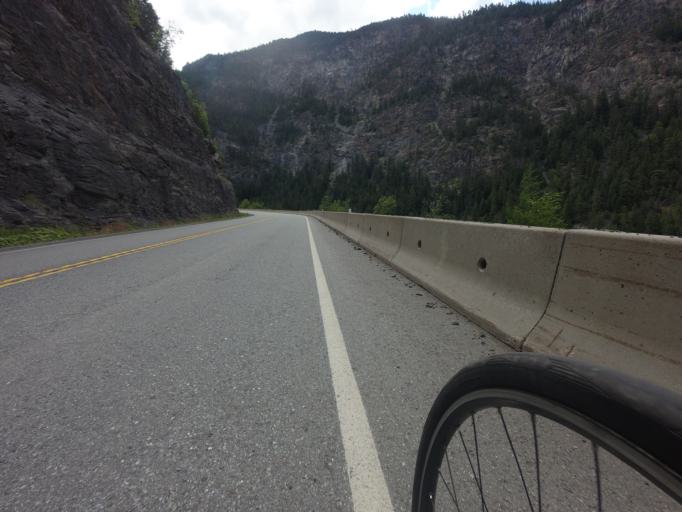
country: CA
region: British Columbia
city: Lillooet
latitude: 50.6464
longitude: -122.0675
